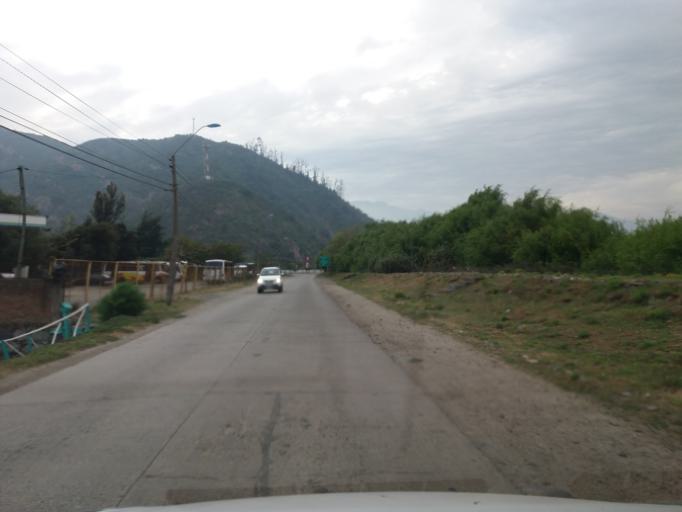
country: CL
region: Valparaiso
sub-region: Provincia de Quillota
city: Hacienda La Calera
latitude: -32.8422
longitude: -71.1056
